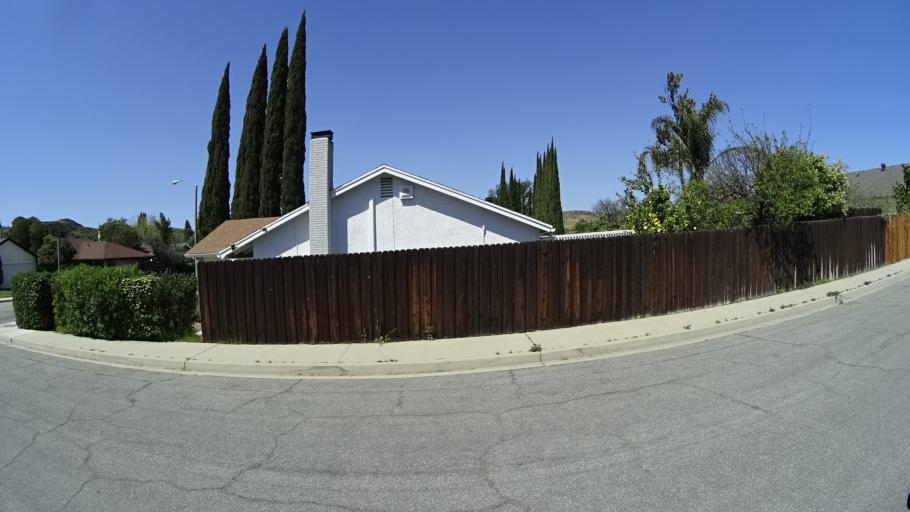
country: US
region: California
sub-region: Ventura County
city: Casa Conejo
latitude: 34.2127
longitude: -118.8894
